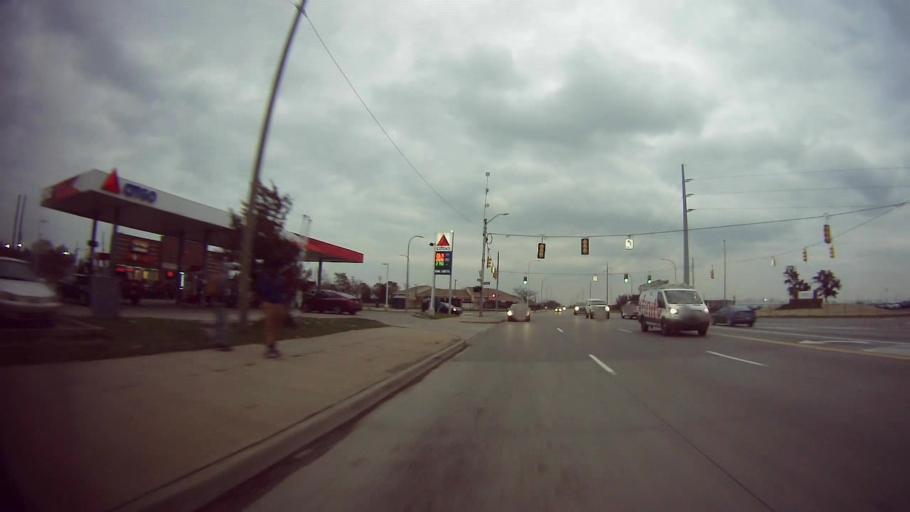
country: US
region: Michigan
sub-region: Wayne County
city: Grosse Pointe Park
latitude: 42.3838
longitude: -82.9677
